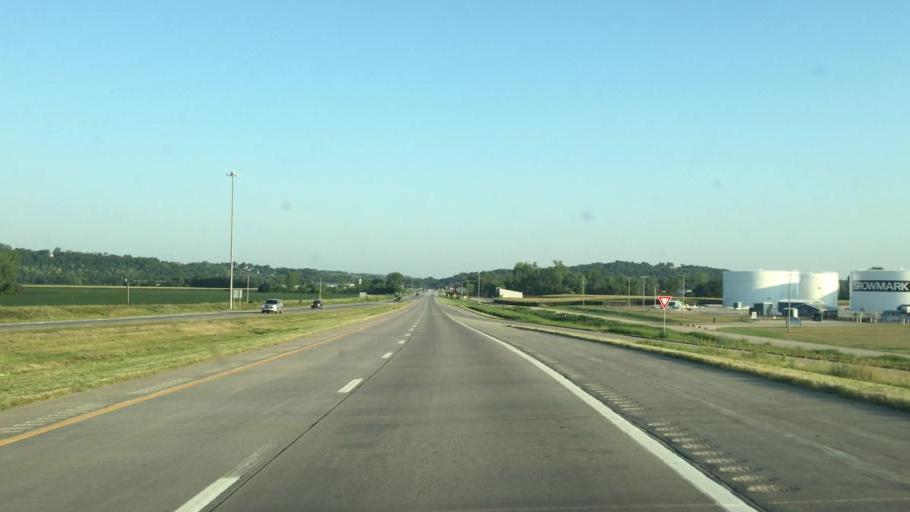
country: US
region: Kansas
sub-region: Doniphan County
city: Wathena
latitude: 39.7485
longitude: -94.9263
